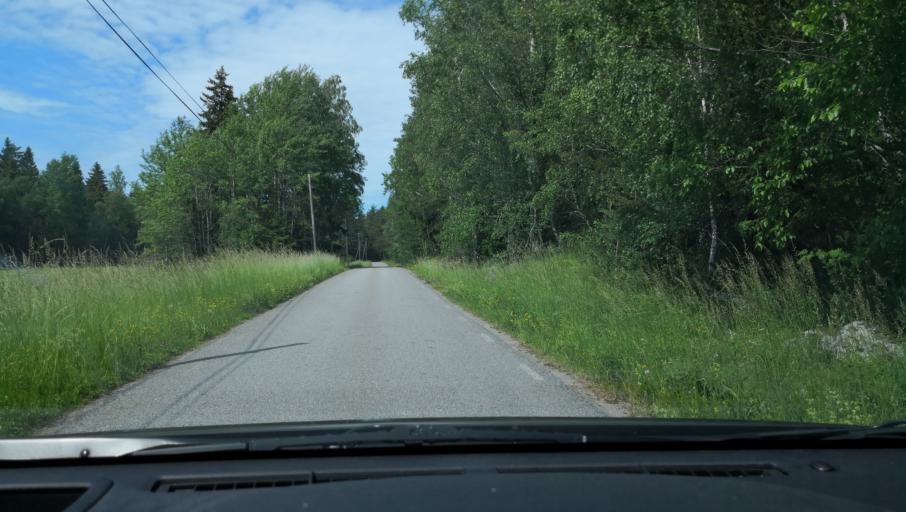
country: SE
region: Stockholm
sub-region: Sigtuna Kommun
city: Sigtuna
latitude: 59.6902
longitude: 17.6479
